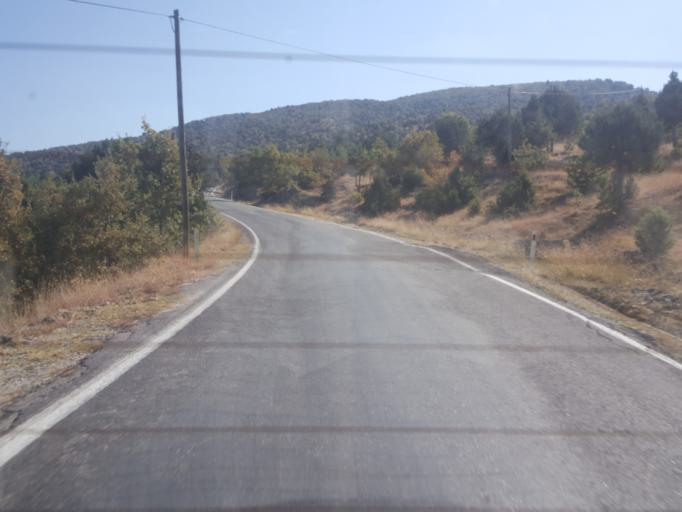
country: TR
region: Kastamonu
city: Tosya
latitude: 40.9916
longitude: 34.1678
